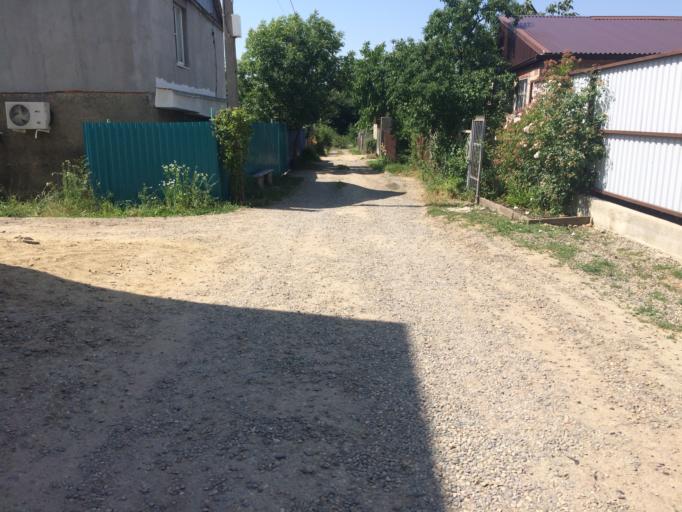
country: RU
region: Stavropol'skiy
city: Tatarka
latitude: 44.9810
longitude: 41.9408
